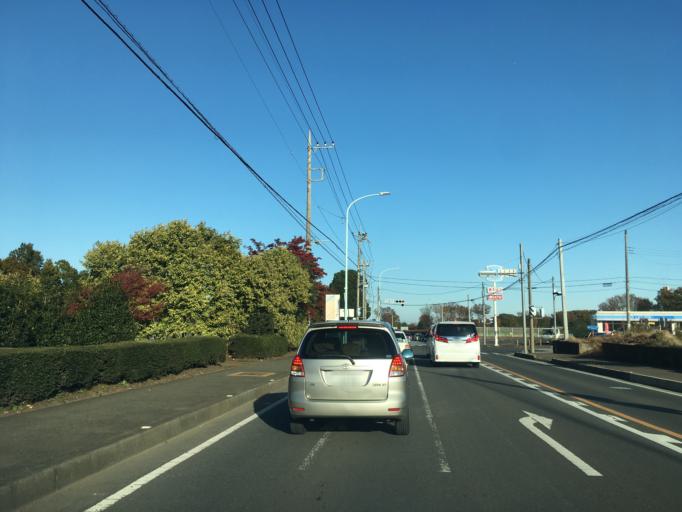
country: JP
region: Saitama
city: Tokorozawa
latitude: 35.8052
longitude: 139.4870
